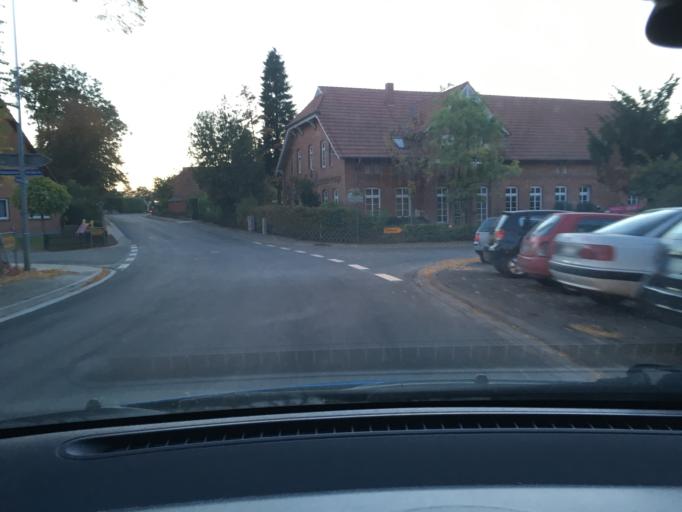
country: DE
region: Lower Saxony
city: Reinstorf
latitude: 53.2411
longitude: 10.5843
